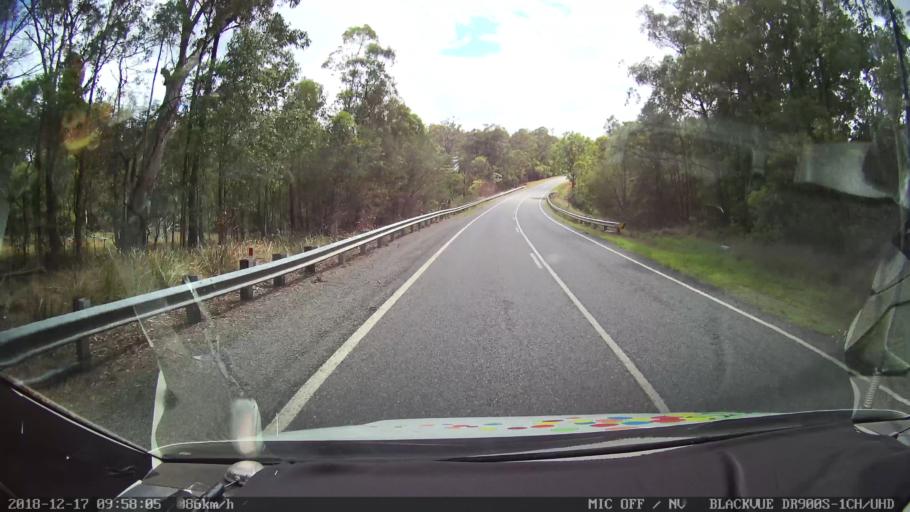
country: AU
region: New South Wales
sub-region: Tenterfield Municipality
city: Carrolls Creek
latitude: -28.9213
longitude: 152.4045
